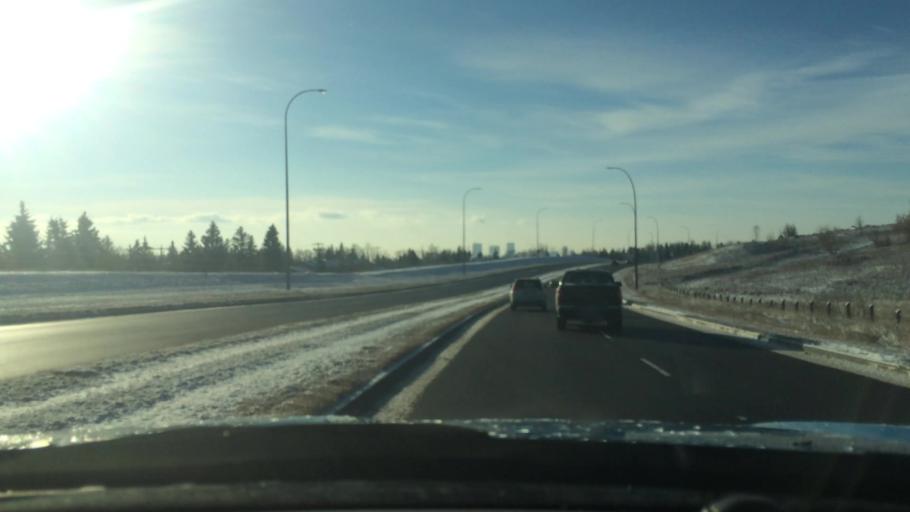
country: CA
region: Alberta
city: Calgary
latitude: 51.1128
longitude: -114.0834
